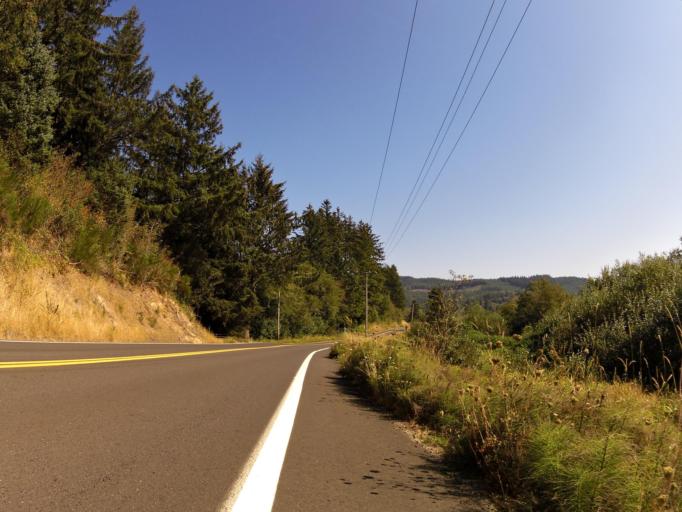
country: US
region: Oregon
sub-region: Tillamook County
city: Pacific City
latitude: 45.1806
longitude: -123.9367
